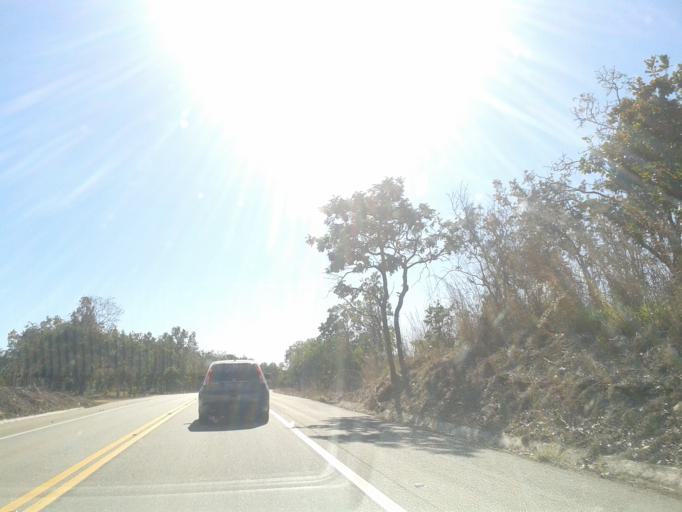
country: BR
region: Goias
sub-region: Itapuranga
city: Itapuranga
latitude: -15.5846
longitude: -50.2662
